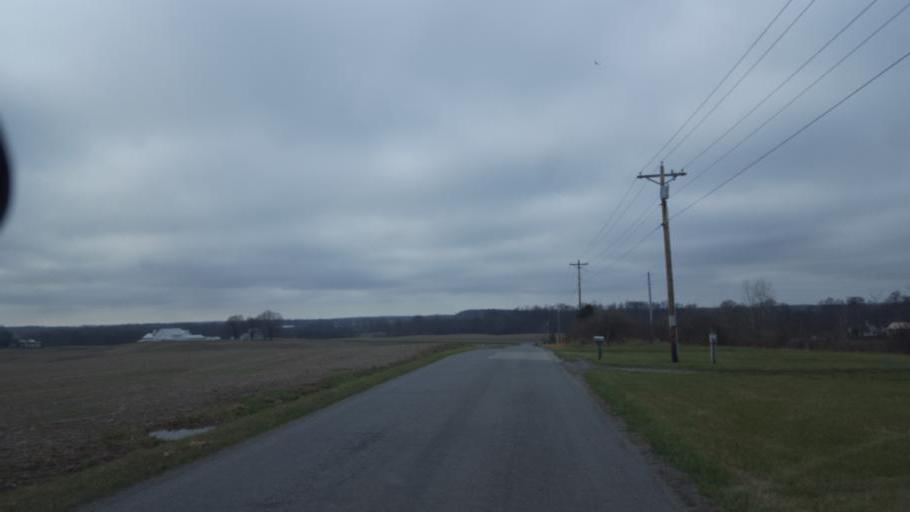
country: US
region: Ohio
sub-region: Knox County
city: Fredericktown
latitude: 40.4715
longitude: -82.6471
